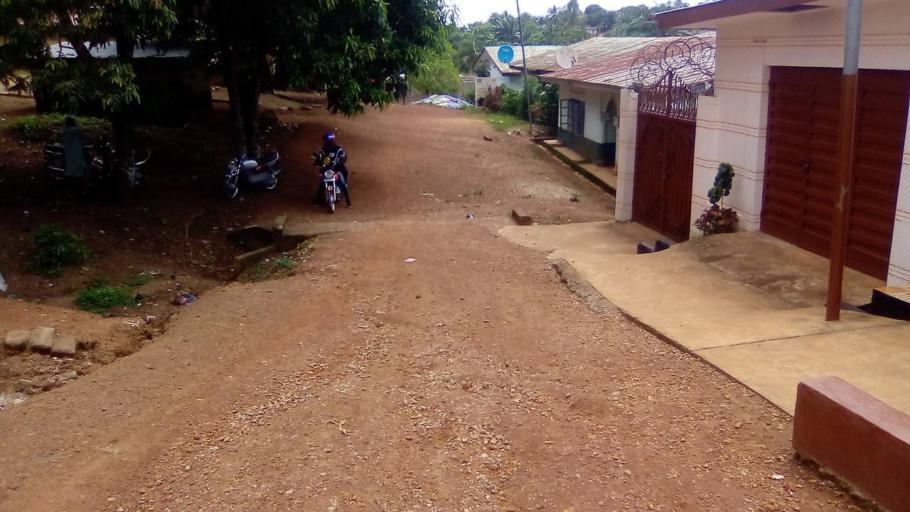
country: SL
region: Southern Province
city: Bo
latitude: 7.9641
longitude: -11.7230
